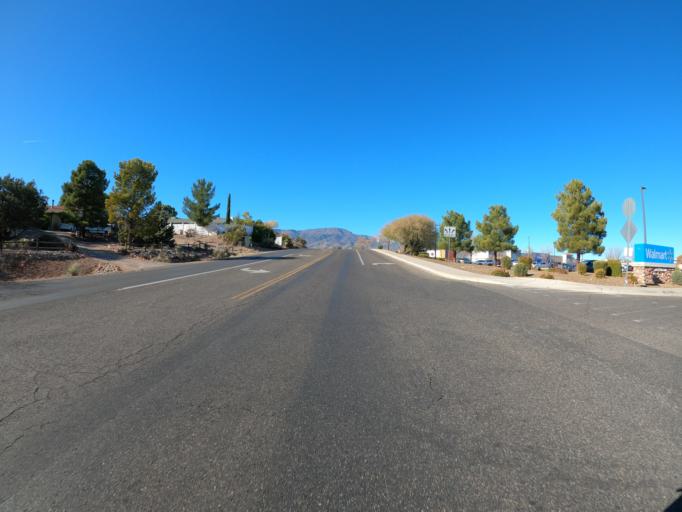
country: US
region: Arizona
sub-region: Yavapai County
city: Verde Village
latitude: 34.7118
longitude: -111.9988
